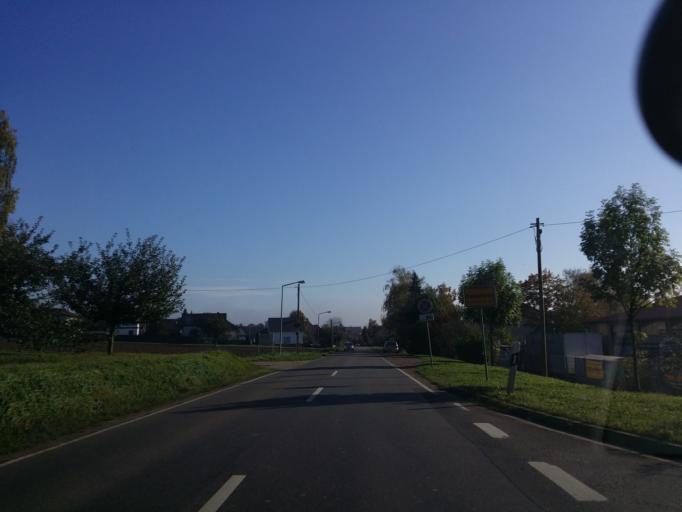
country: DE
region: Rheinland-Pfalz
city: Biebelnheim
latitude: 49.7948
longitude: 8.1643
